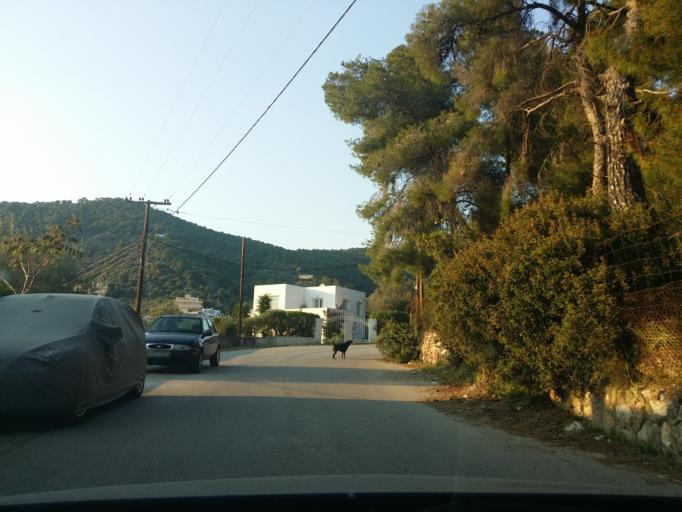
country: GR
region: Attica
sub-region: Nomos Piraios
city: Poros
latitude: 37.5069
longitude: 23.4727
